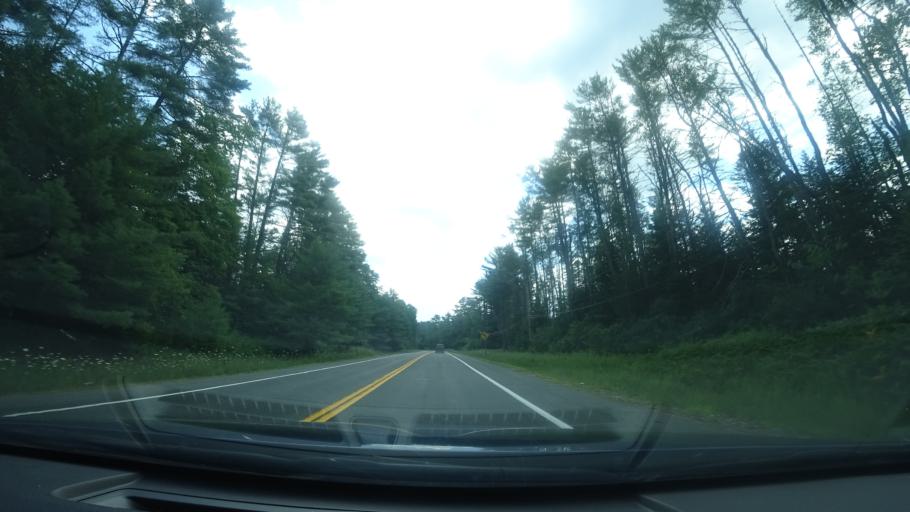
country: US
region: New York
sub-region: Warren County
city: Warrensburg
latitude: 43.6586
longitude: -73.8157
